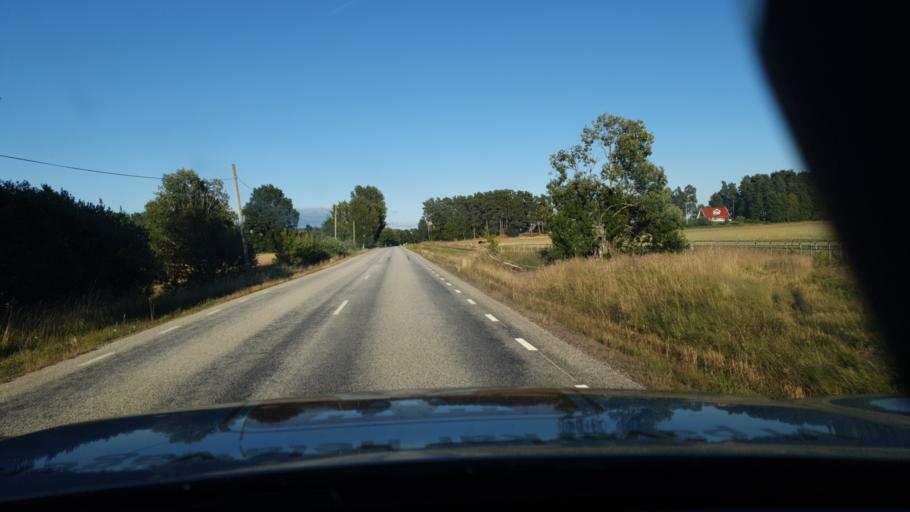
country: SE
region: Vaestra Goetaland
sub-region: Skovde Kommun
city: Stopen
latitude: 58.4793
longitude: 13.8796
